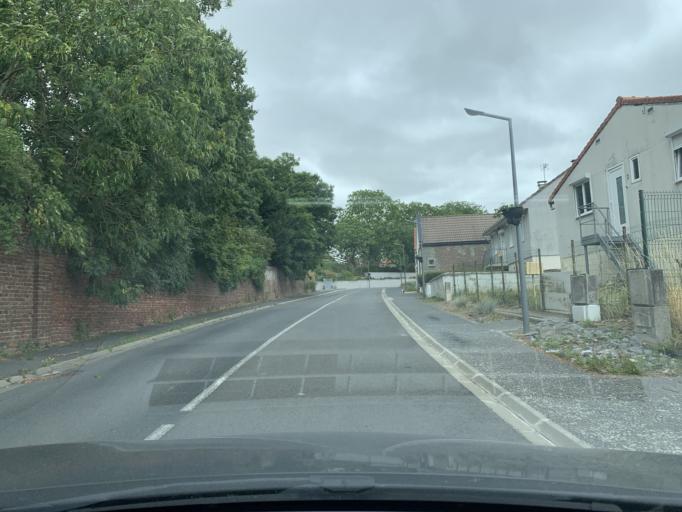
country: FR
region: Nord-Pas-de-Calais
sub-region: Departement du Nord
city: Neuville-Saint-Remy
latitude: 50.1975
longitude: 3.2170
